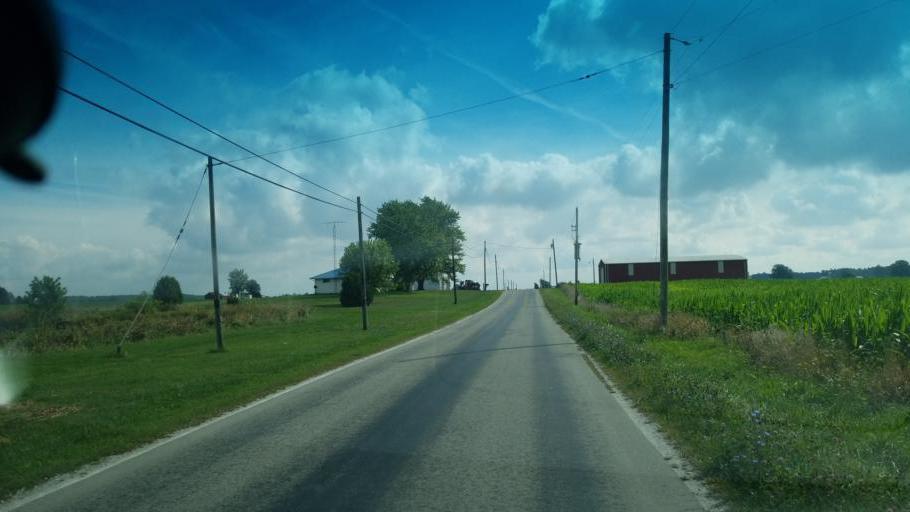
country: US
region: Ohio
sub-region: Hardin County
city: Forest
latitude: 40.8615
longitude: -83.4532
